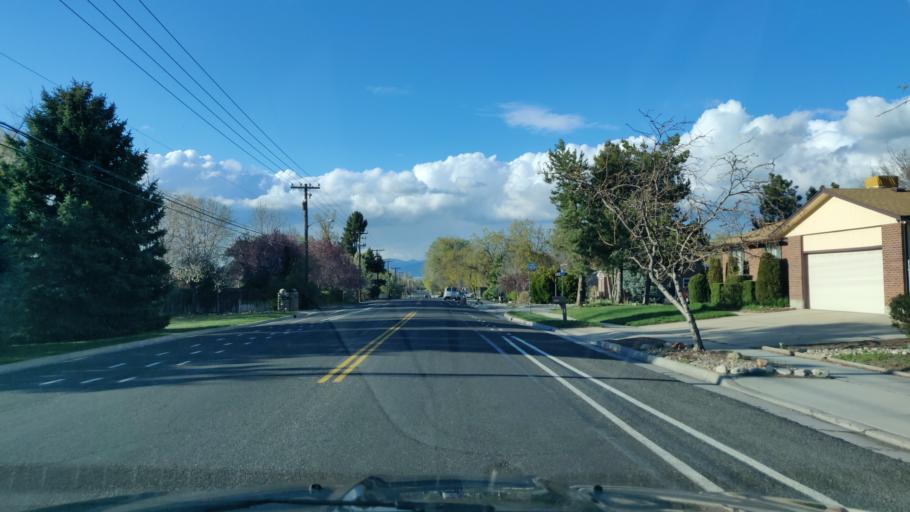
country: US
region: Utah
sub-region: Salt Lake County
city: Cottonwood Heights
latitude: 40.6307
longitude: -111.8247
